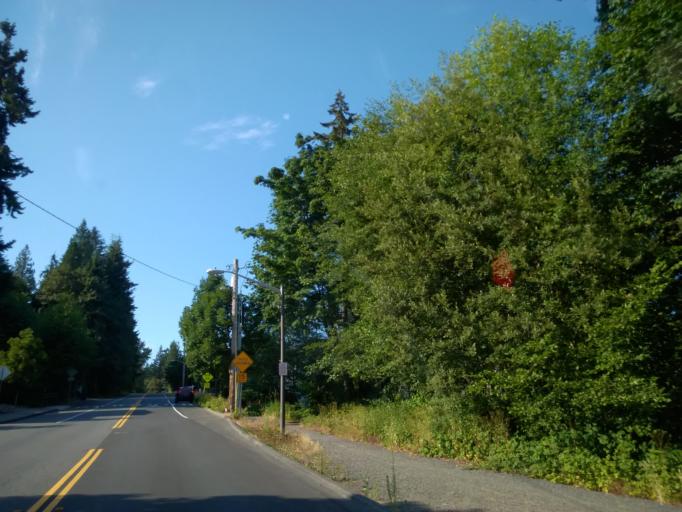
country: US
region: Washington
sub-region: King County
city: Woodinville
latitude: 47.7731
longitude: -122.1586
